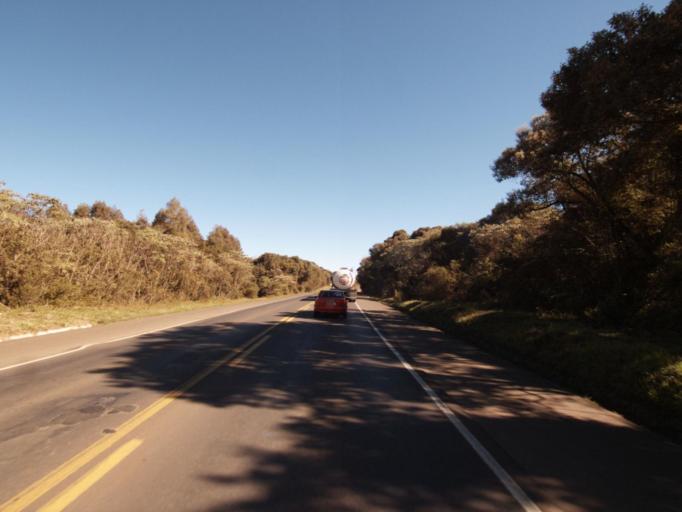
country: BR
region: Santa Catarina
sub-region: Xanxere
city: Xanxere
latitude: -26.8719
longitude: -52.2768
